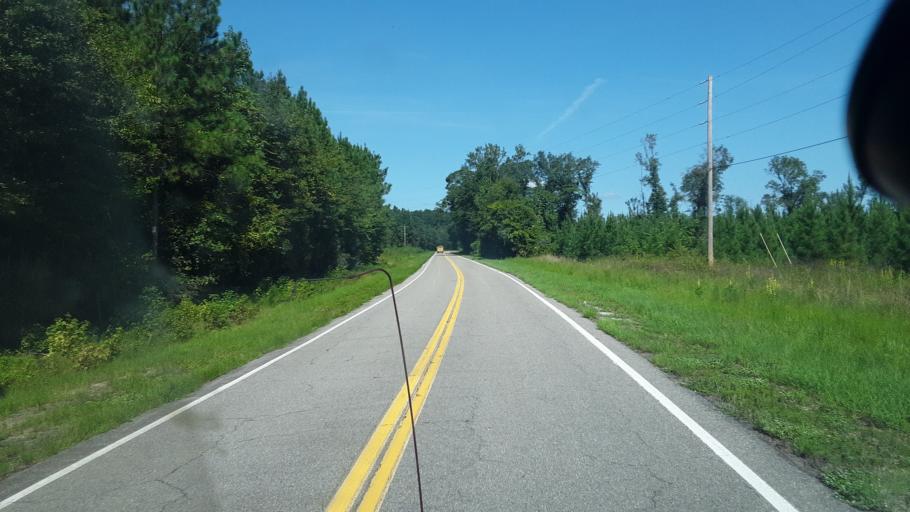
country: US
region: South Carolina
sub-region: Hampton County
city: Varnville
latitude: 32.9517
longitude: -81.0354
